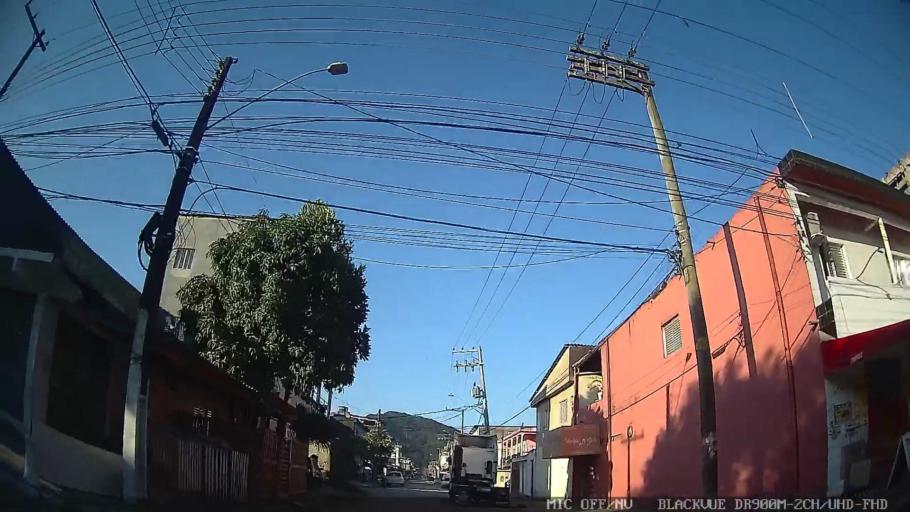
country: BR
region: Sao Paulo
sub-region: Guaruja
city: Guaruja
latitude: -23.9610
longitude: -46.2500
